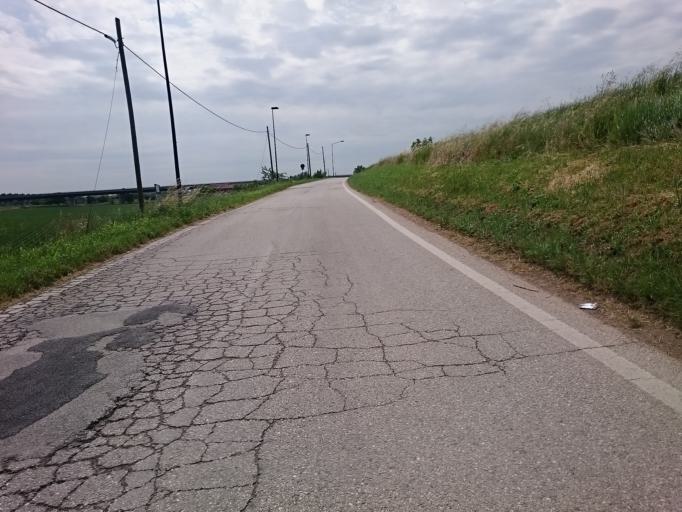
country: IT
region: Veneto
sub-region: Provincia di Padova
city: Este
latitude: 45.2069
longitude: 11.6489
